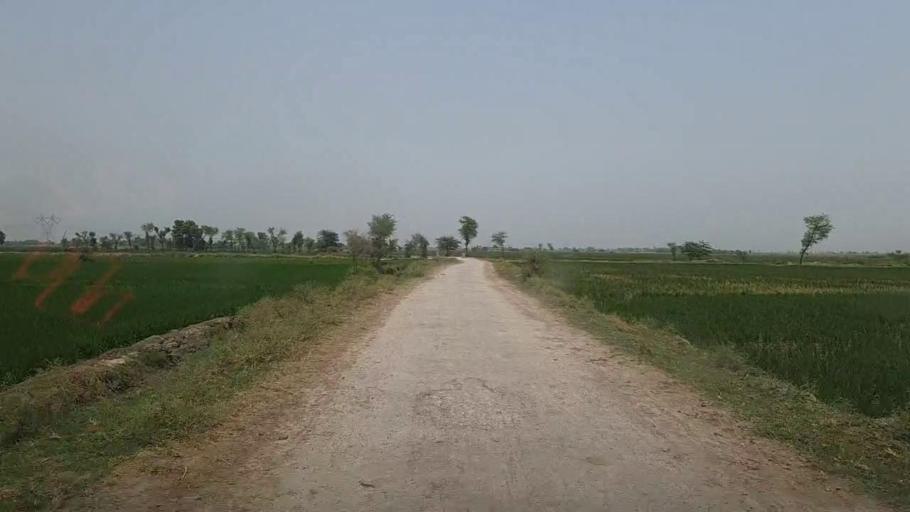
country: PK
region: Sindh
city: Sita Road
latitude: 27.0609
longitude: 67.8491
